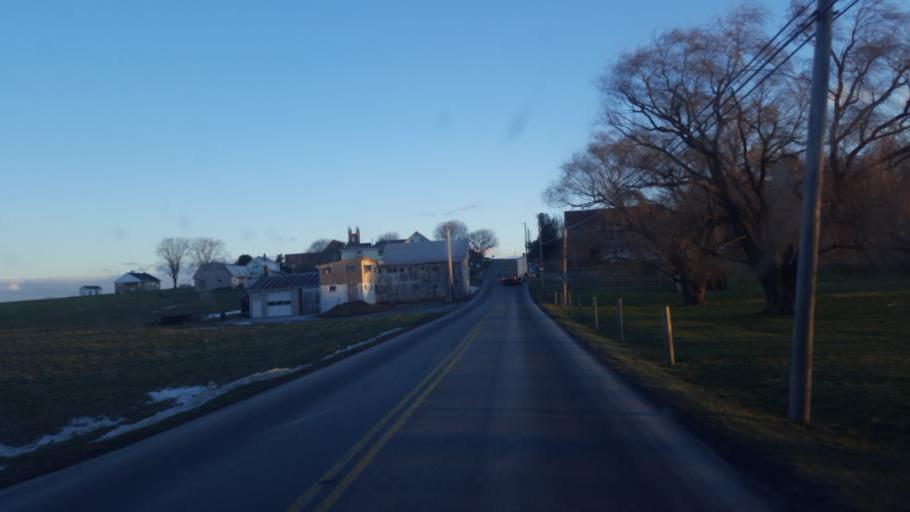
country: US
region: Pennsylvania
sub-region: Lancaster County
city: Intercourse
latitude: 40.0716
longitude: -76.1054
